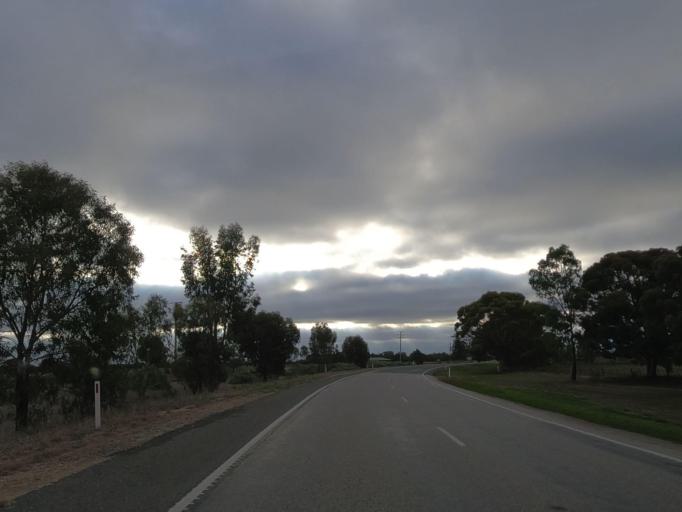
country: AU
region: Victoria
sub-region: Swan Hill
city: Swan Hill
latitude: -35.7292
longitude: 143.8926
